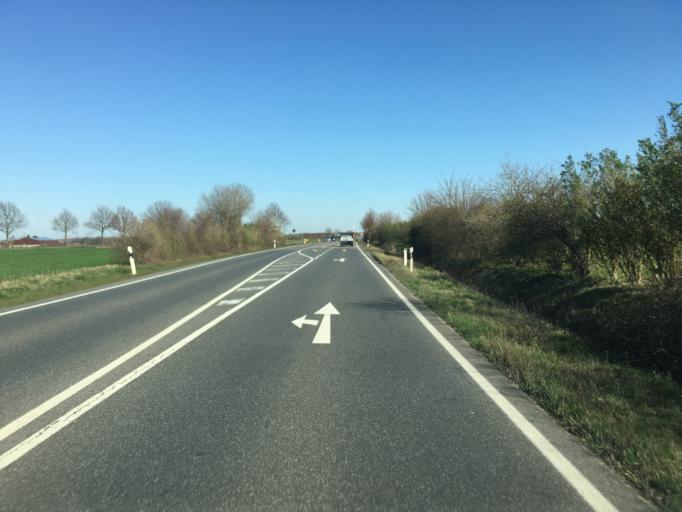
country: DE
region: North Rhine-Westphalia
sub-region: Regierungsbezirk Koln
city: Kerpen
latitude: 50.8522
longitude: 6.6699
